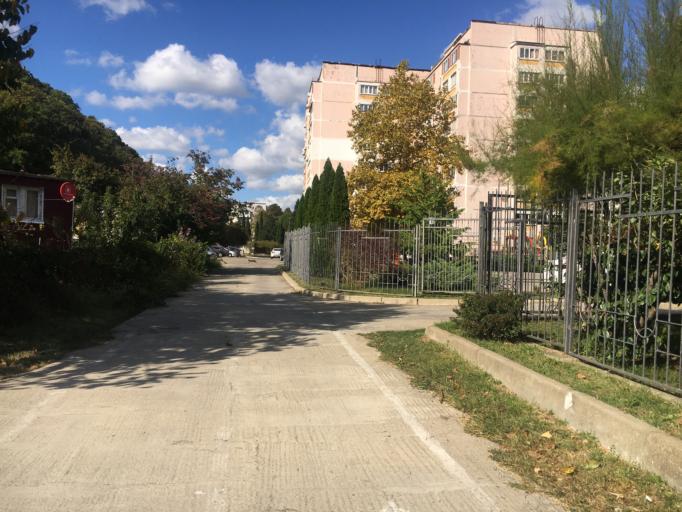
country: RU
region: Krasnodarskiy
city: Nebug
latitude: 44.1787
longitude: 38.9738
